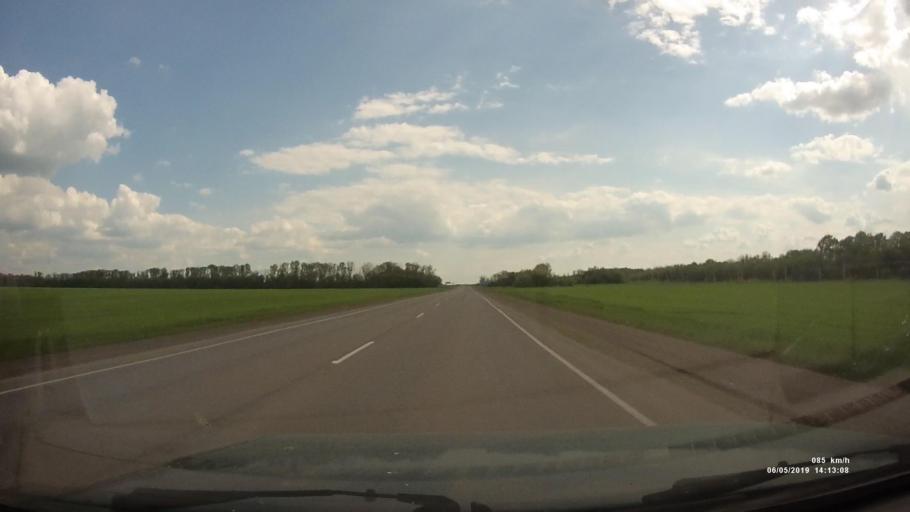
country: RU
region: Rostov
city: Kamenolomni
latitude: 47.6637
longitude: 40.2925
